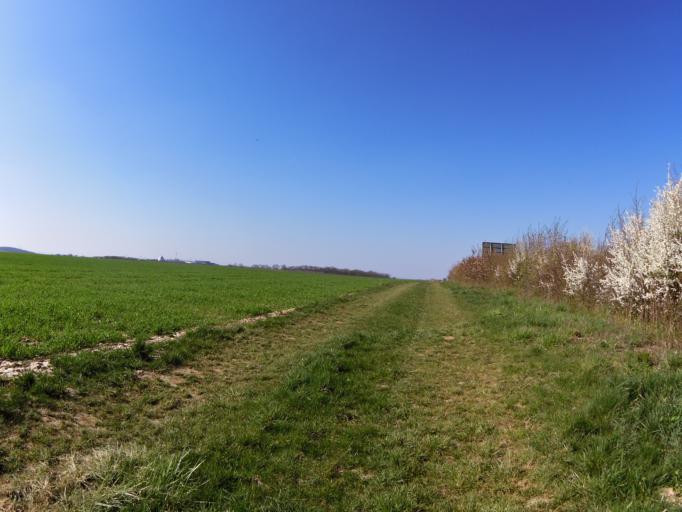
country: DE
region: Bavaria
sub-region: Regierungsbezirk Unterfranken
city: Biebelried
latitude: 49.7655
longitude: 10.1022
